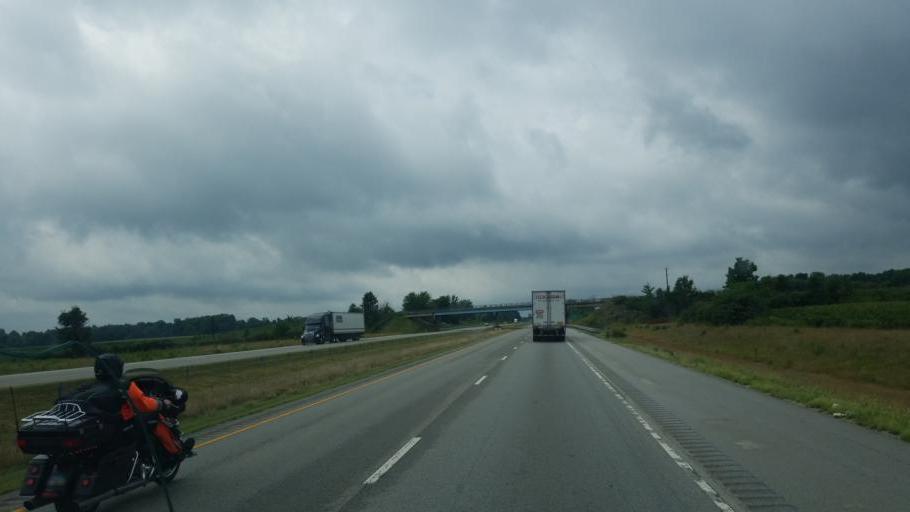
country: US
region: Indiana
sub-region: Clay County
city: Brazil
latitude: 39.4796
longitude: -87.0128
